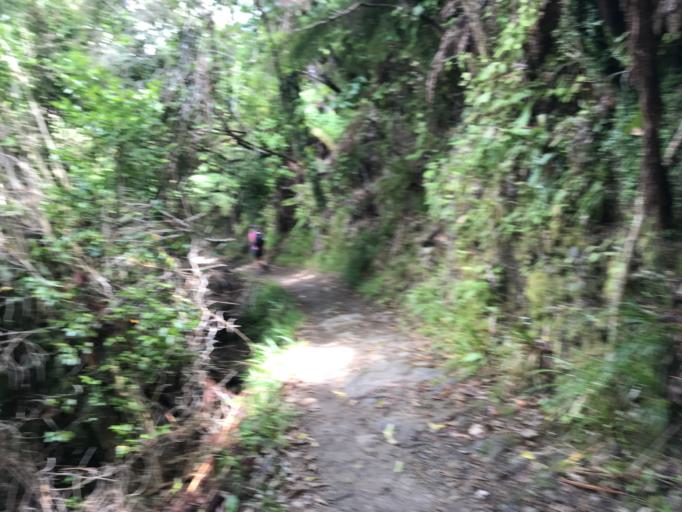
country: NZ
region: Marlborough
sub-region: Marlborough District
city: Picton
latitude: -41.2528
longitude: 173.9507
